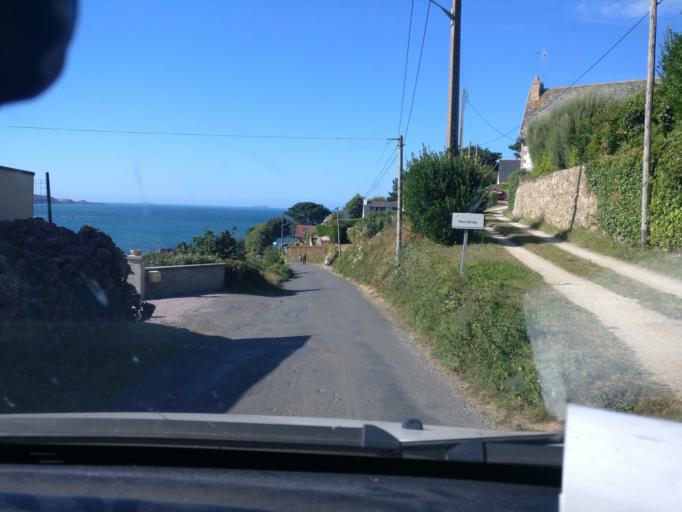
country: FR
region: Brittany
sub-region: Departement des Cotes-d'Armor
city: Trelevern
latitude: 48.8161
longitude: -3.3697
